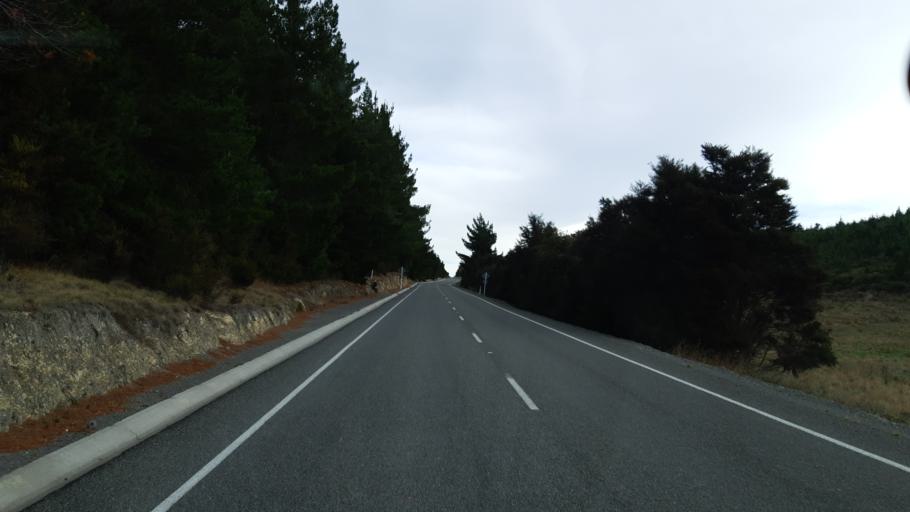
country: NZ
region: Tasman
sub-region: Tasman District
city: Brightwater
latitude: -41.6570
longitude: 173.2307
